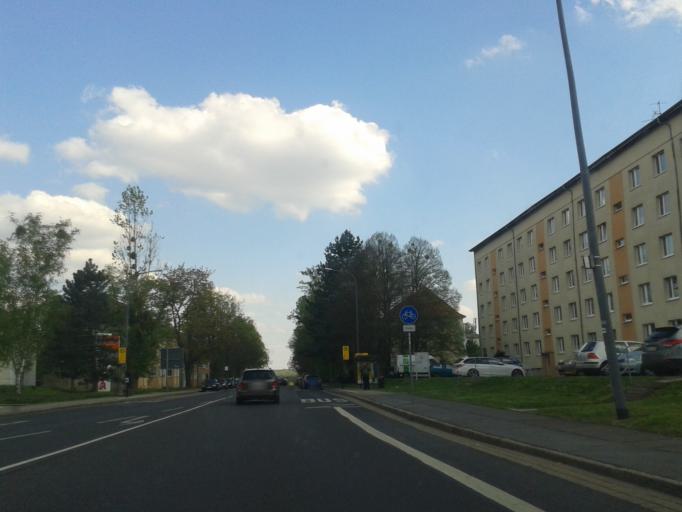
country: DE
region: Saxony
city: Albertstadt
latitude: 51.1184
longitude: 13.7668
